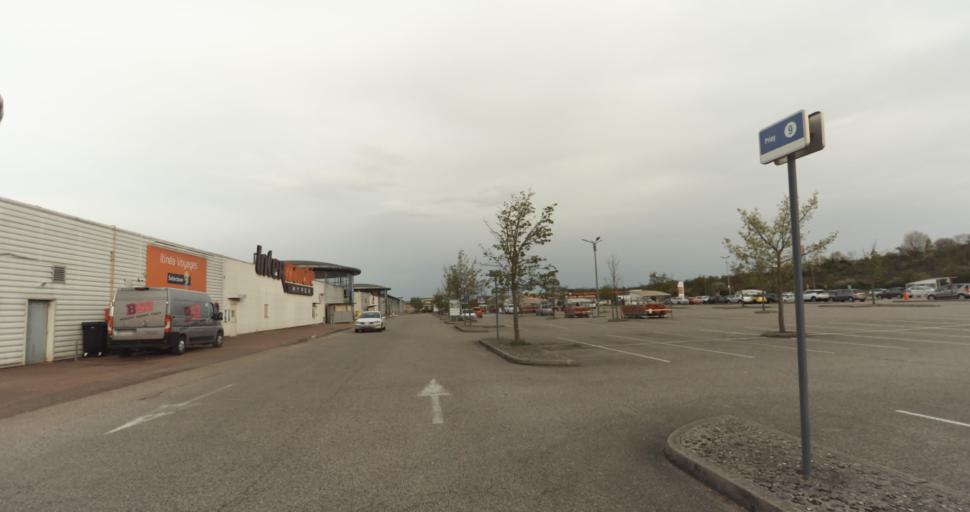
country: FR
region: Rhone-Alpes
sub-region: Departement de l'Ain
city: Amberieu-en-Bugey
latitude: 45.9718
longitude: 5.3390
